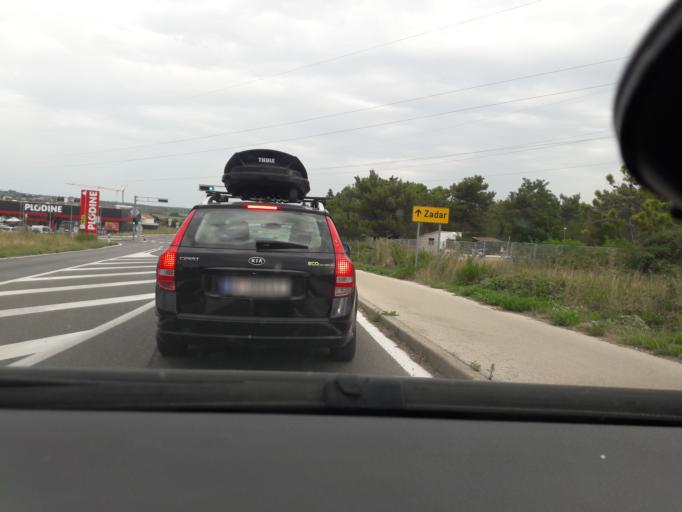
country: HR
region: Zadarska
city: Nin
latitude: 44.2395
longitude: 15.1717
